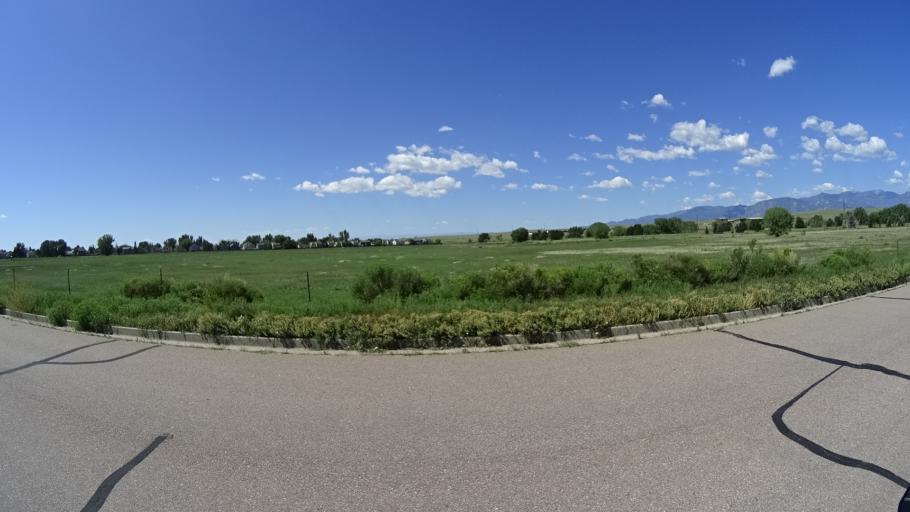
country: US
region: Colorado
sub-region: El Paso County
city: Security-Widefield
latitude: 38.7729
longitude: -104.6556
